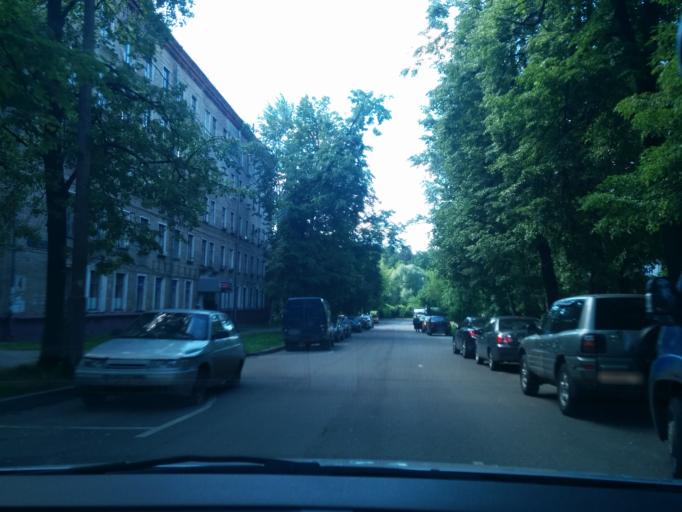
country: RU
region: Moskovskaya
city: Izmaylovo
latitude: 55.7904
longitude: 37.8149
